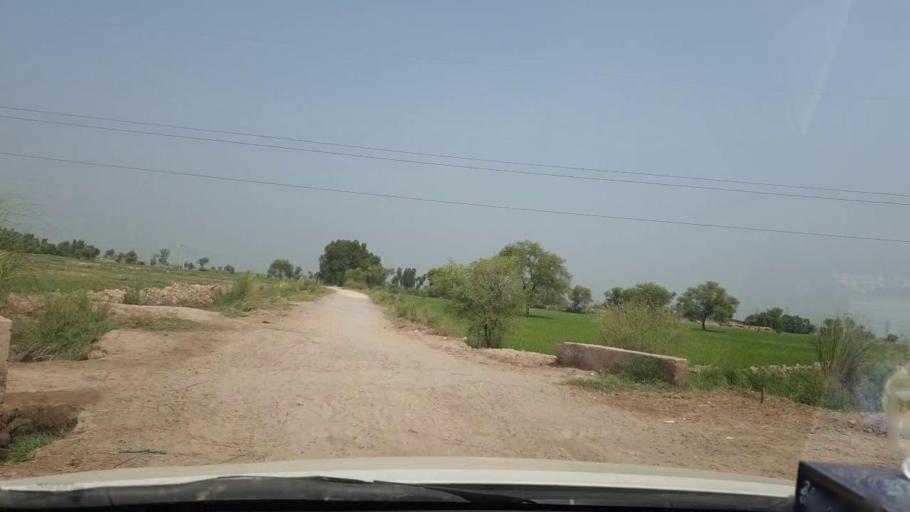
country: PK
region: Sindh
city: Shikarpur
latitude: 27.9885
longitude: 68.6976
